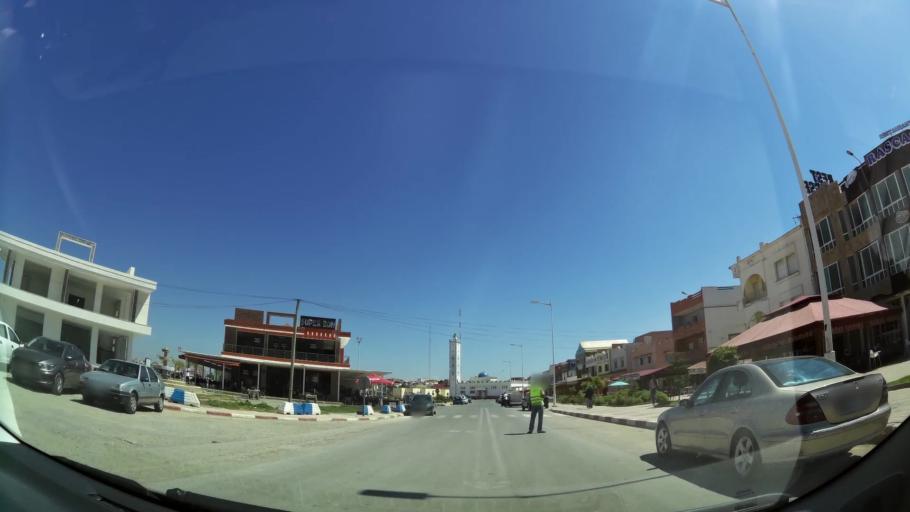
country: MA
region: Oriental
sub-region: Berkane-Taourirt
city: Madagh
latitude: 35.1425
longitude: -2.4240
